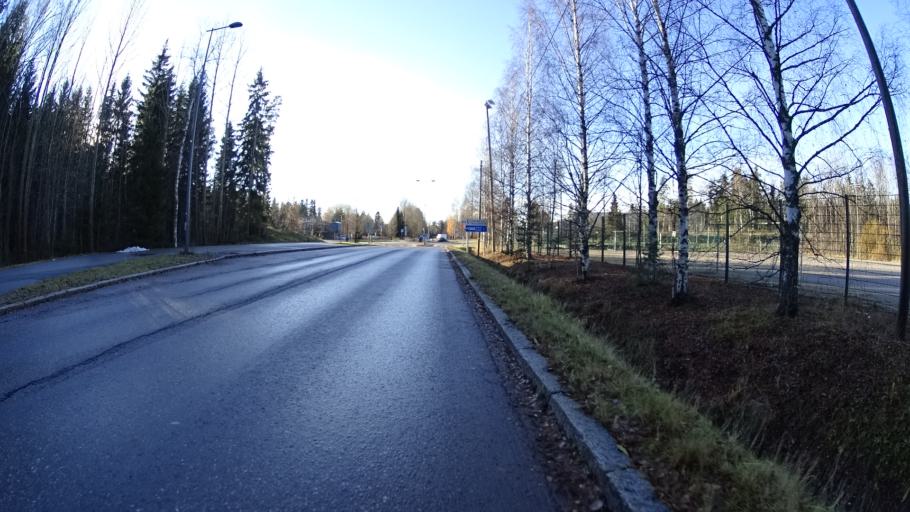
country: FI
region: Uusimaa
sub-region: Helsinki
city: Kilo
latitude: 60.2382
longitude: 24.8233
